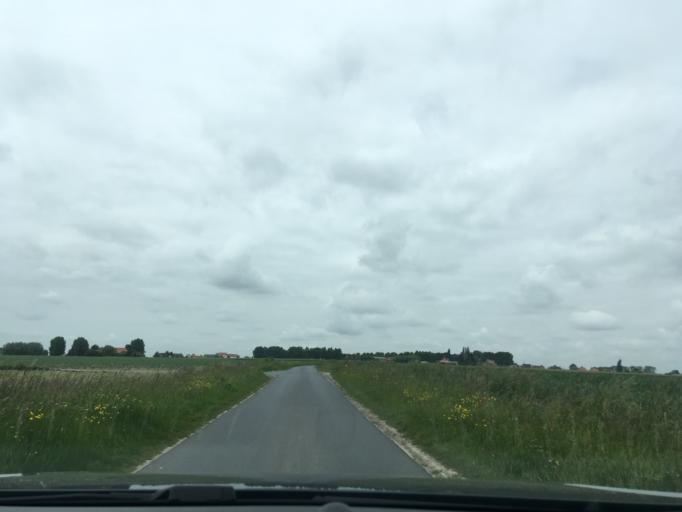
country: BE
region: Flanders
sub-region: Provincie West-Vlaanderen
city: Moorslede
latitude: 50.8411
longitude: 3.0730
